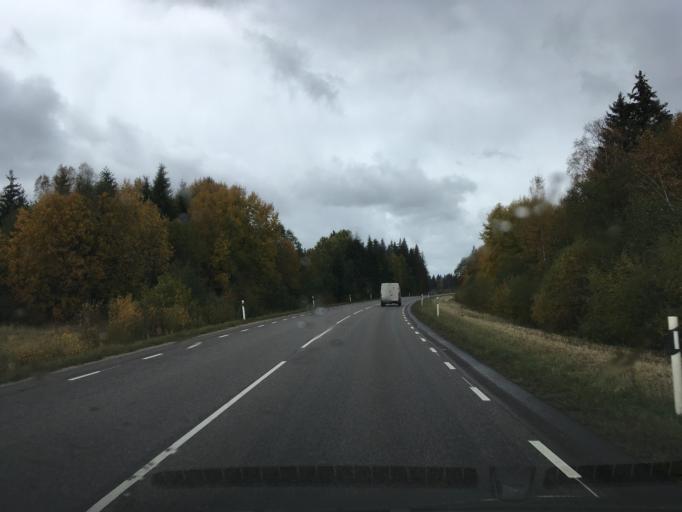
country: EE
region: Harju
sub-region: Anija vald
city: Kehra
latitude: 59.3333
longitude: 25.3131
